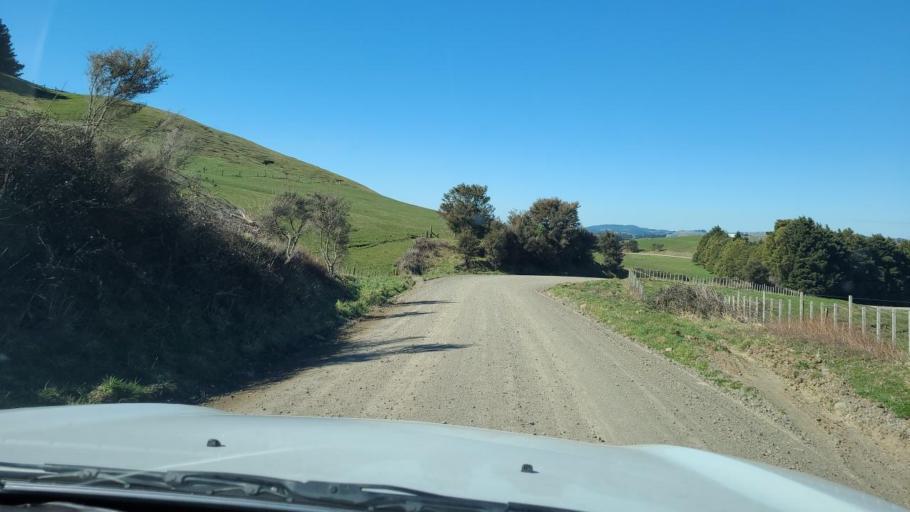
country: NZ
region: Hawke's Bay
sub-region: Napier City
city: Taradale
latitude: -39.4209
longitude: 176.4963
